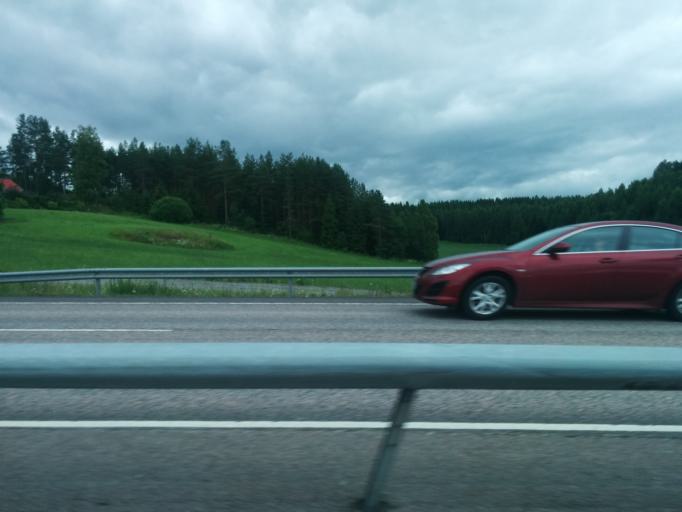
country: FI
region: Pirkanmaa
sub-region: Tampere
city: Orivesi
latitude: 61.6932
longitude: 24.4115
